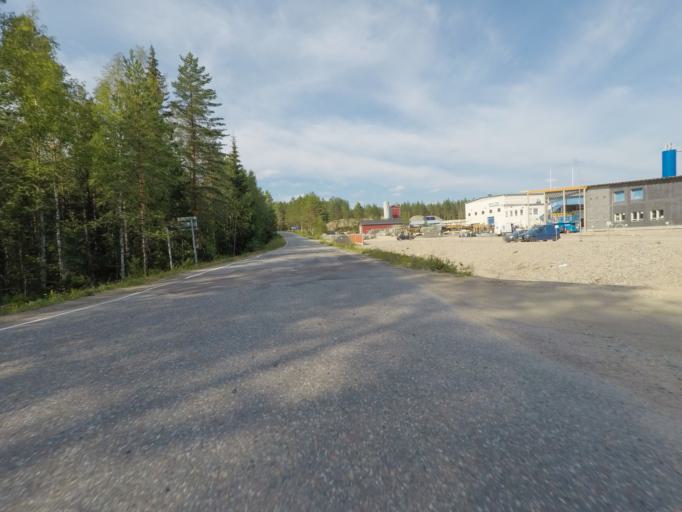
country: FI
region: Southern Savonia
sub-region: Savonlinna
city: Sulkava
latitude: 61.7861
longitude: 28.2427
